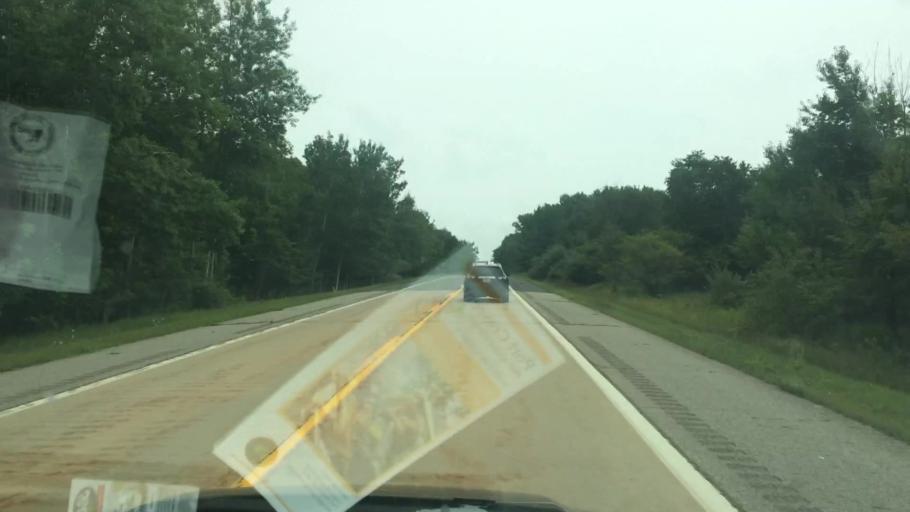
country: US
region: Michigan
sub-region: Huron County
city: Harbor Beach
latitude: 44.0257
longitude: -82.8221
